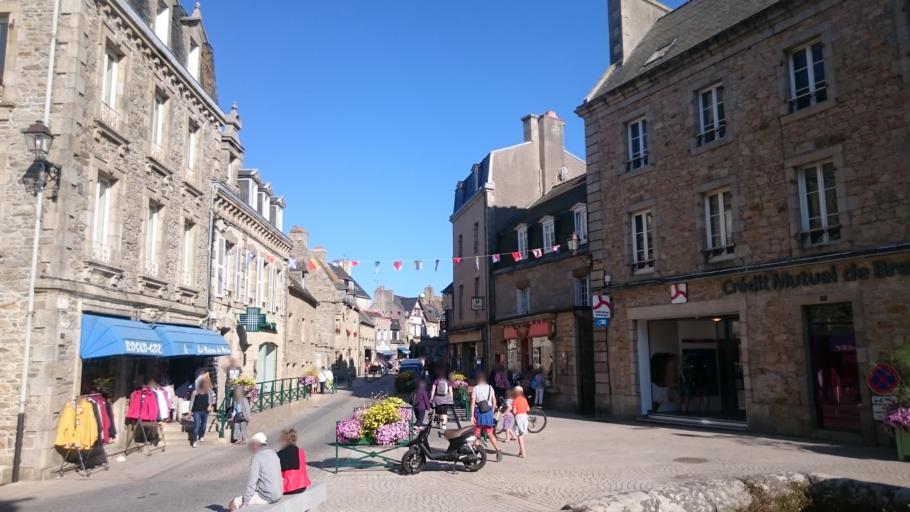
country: FR
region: Brittany
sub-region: Departement du Finistere
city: Roscoff
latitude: 48.7265
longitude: -3.9853
